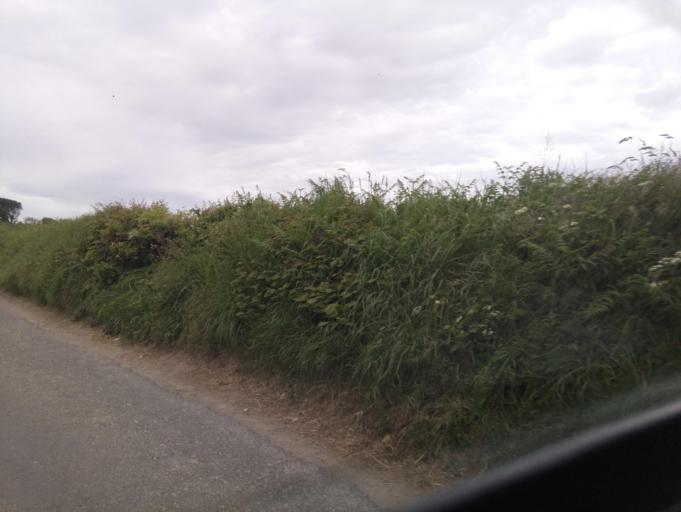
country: GB
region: England
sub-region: Devon
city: Dartmouth
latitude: 50.3482
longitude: -3.6580
